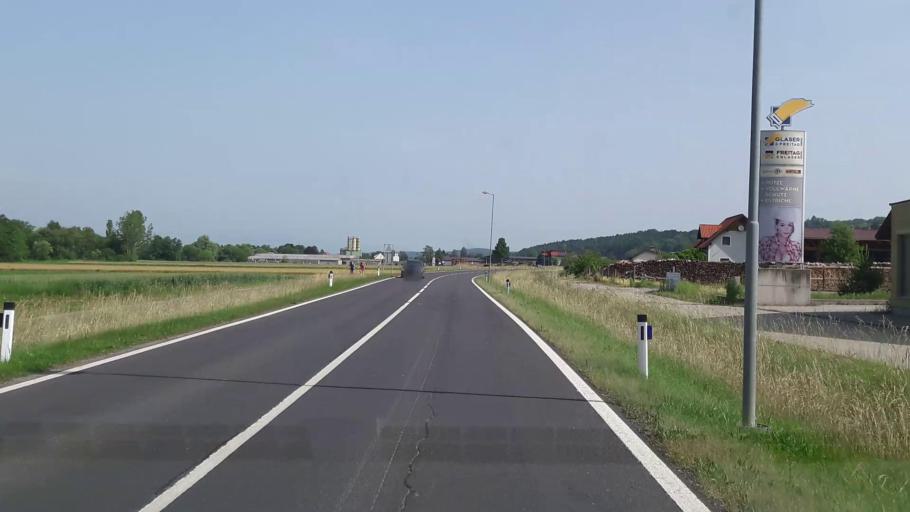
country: AT
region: Styria
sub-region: Politischer Bezirk Hartberg-Fuerstenfeld
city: Burgau
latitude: 47.1438
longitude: 16.1177
